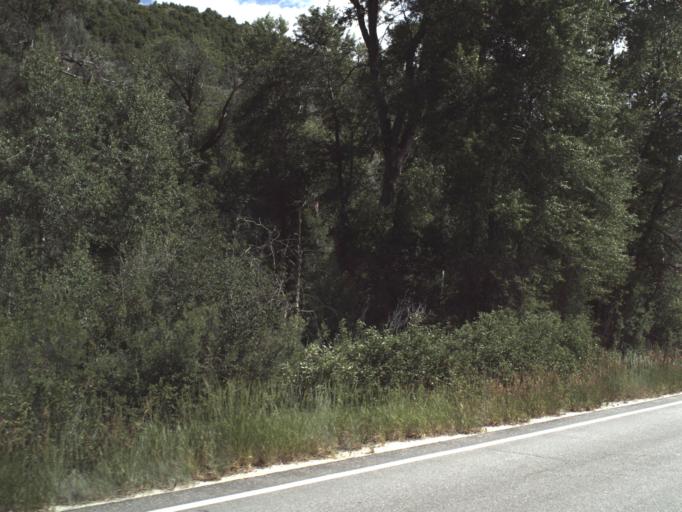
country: US
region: Utah
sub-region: Weber County
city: Wolf Creek
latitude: 41.3129
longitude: -111.6153
